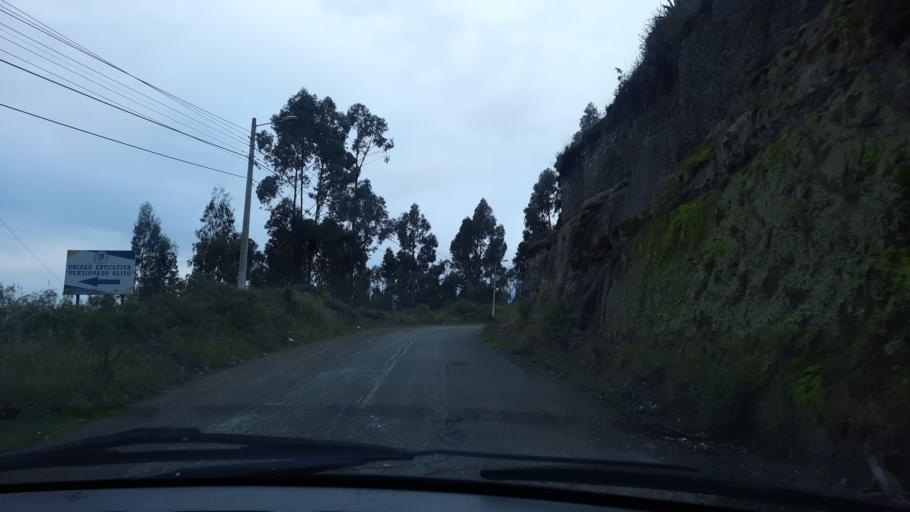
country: EC
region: Chimborazo
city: Riobamba
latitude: -1.6840
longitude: -78.6609
